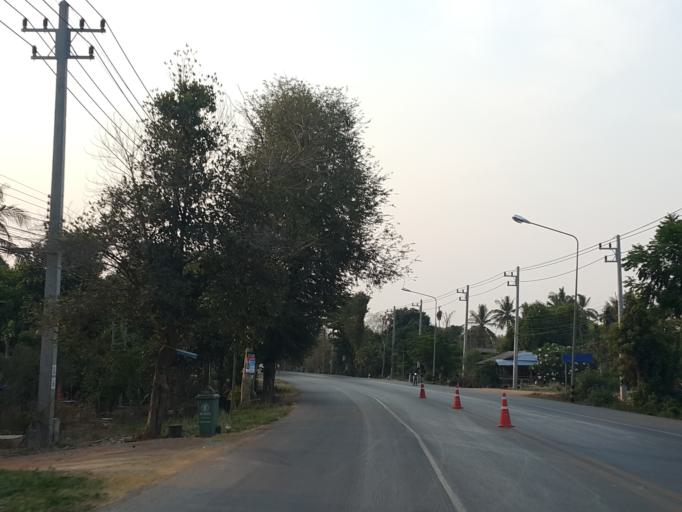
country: TH
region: Sukhothai
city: Sawankhalok
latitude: 17.2517
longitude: 99.8580
